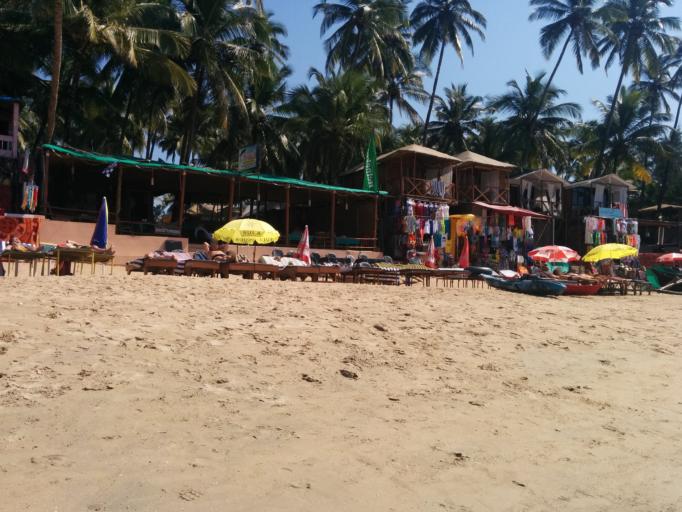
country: IN
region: Karnataka
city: Canacona
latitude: 15.0059
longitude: 74.0269
